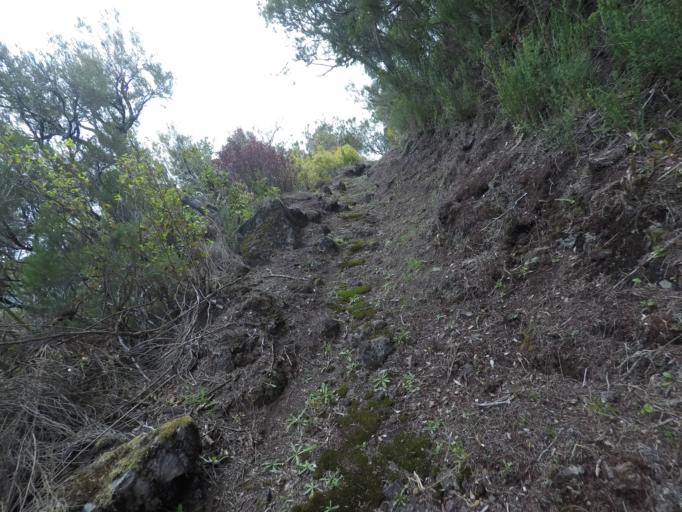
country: PT
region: Madeira
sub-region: Camara de Lobos
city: Curral das Freiras
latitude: 32.7672
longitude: -16.9754
